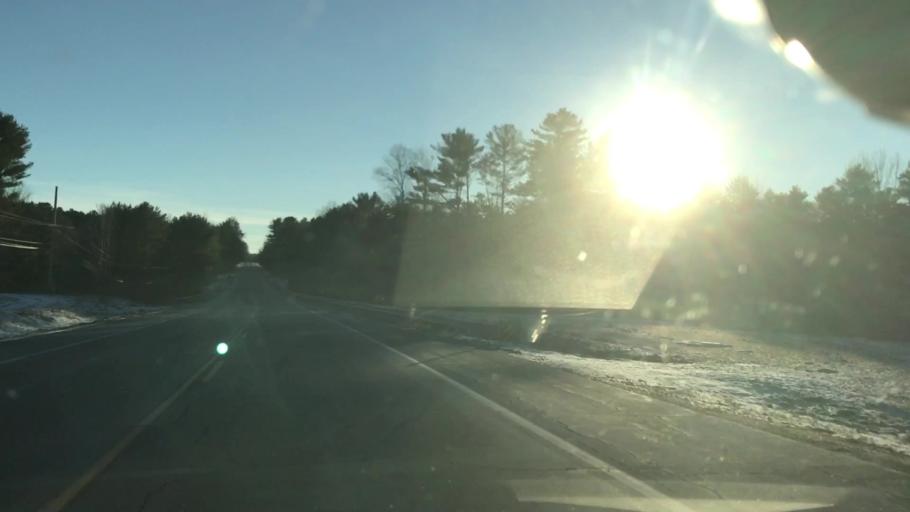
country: US
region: New Hampshire
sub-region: Grafton County
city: Lyme
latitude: 43.8031
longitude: -72.1661
